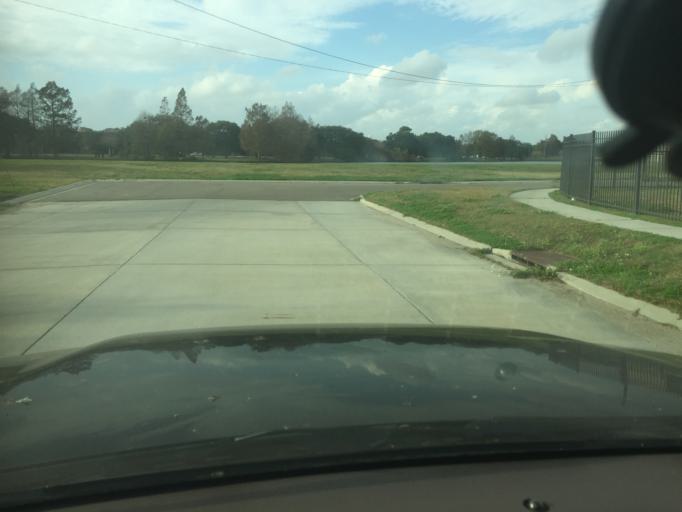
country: US
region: Louisiana
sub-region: Orleans Parish
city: New Orleans
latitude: 29.9962
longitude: -90.0840
